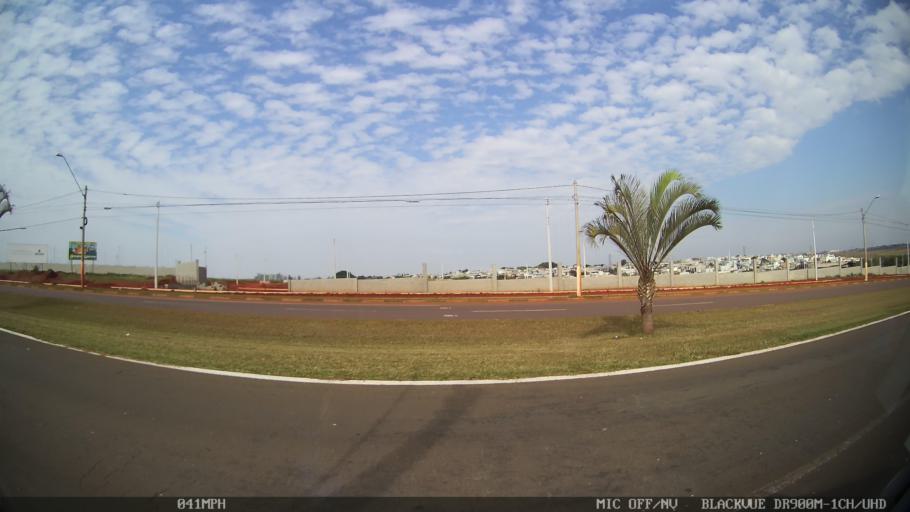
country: BR
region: Sao Paulo
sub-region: Paulinia
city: Paulinia
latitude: -22.7942
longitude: -47.1434
